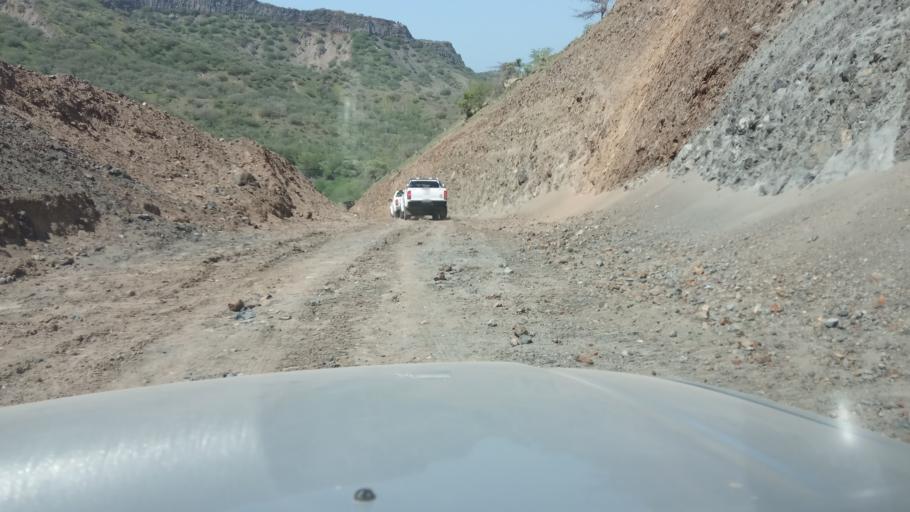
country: CV
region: Santa Catarina
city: Assomada
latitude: 15.1156
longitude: -23.7292
